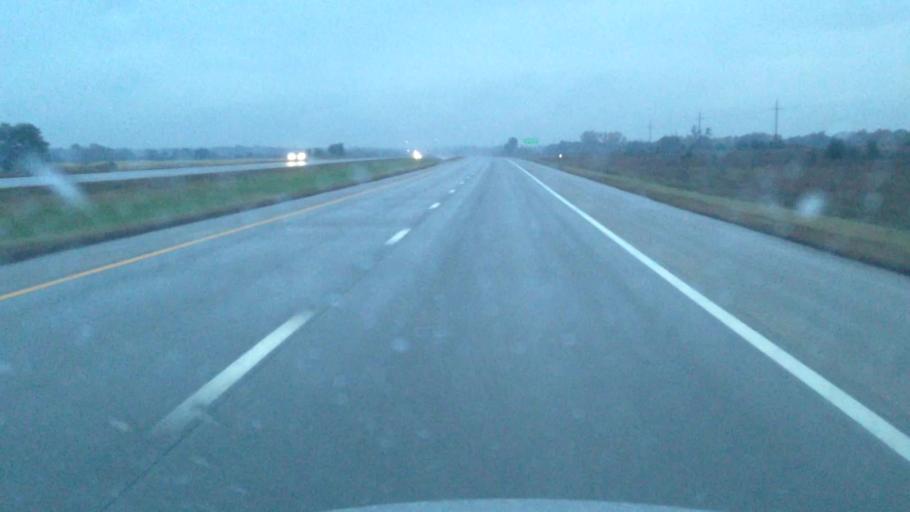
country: US
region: Kansas
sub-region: Douglas County
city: Baldwin City
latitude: 38.7334
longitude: -95.2683
